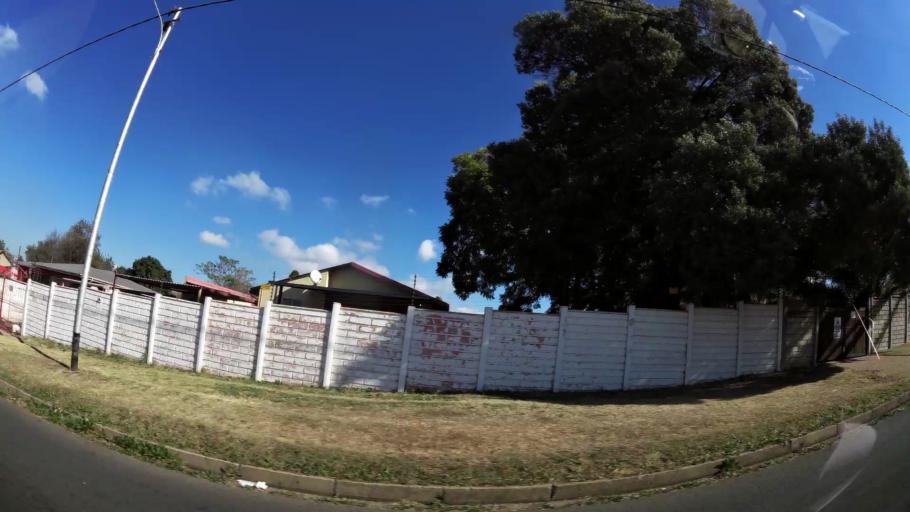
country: ZA
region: Gauteng
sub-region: City of Johannesburg Metropolitan Municipality
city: Roodepoort
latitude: -26.1477
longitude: 27.8338
